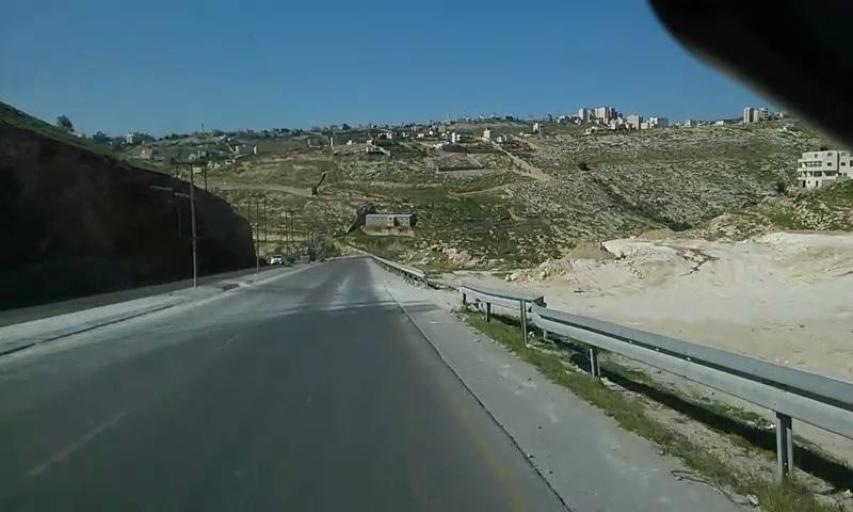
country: PS
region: West Bank
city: Abu Dis
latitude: 31.7515
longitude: 35.2783
